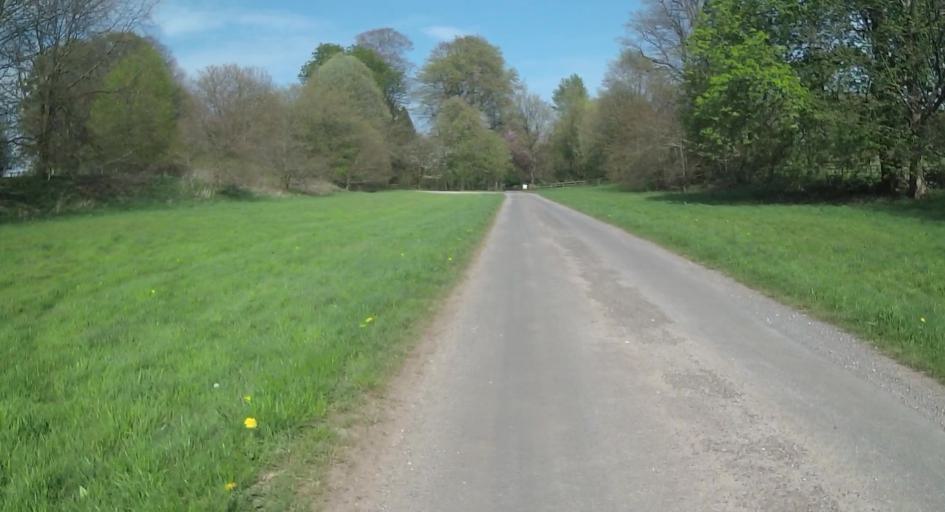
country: GB
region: England
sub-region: Hampshire
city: Basingstoke
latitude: 51.1968
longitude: -1.1567
